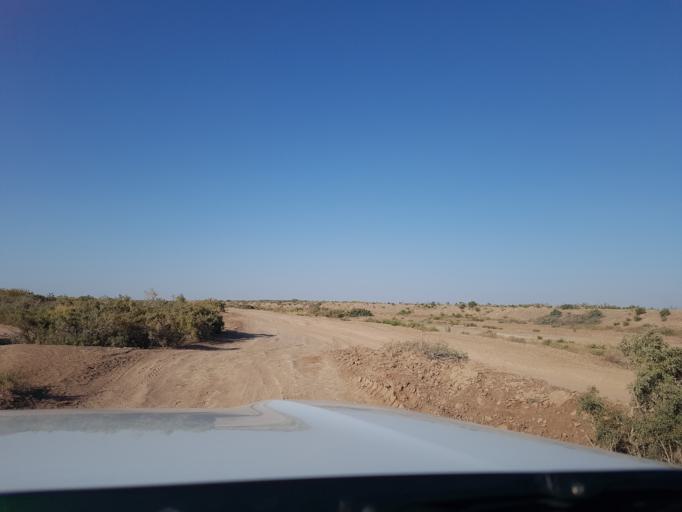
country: IR
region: Razavi Khorasan
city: Sarakhs
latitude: 36.9813
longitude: 61.3858
